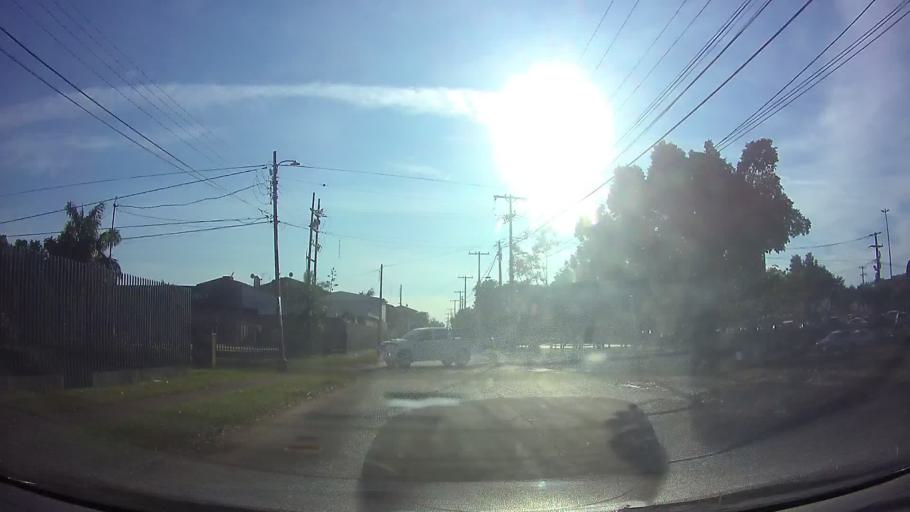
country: PY
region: Central
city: San Lorenzo
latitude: -25.2647
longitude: -57.5031
